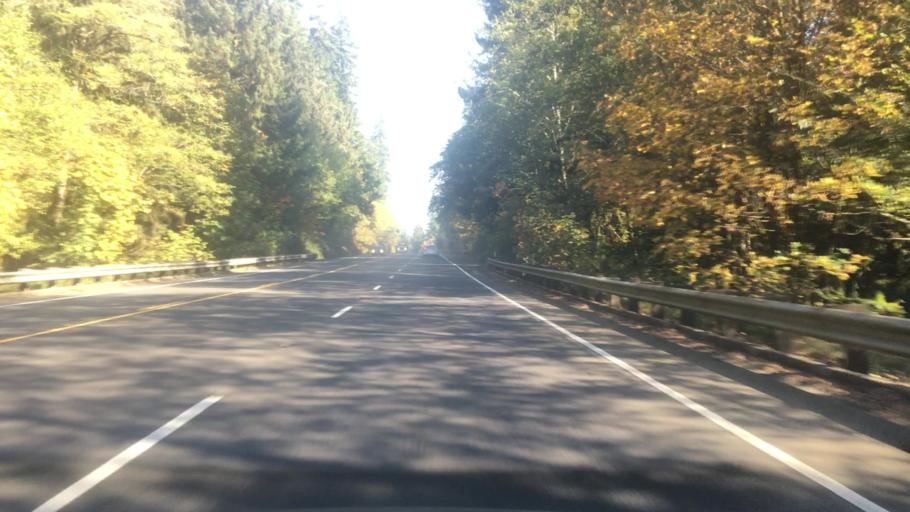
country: US
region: Oregon
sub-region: Lincoln County
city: Rose Lodge
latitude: 45.0483
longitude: -123.7917
